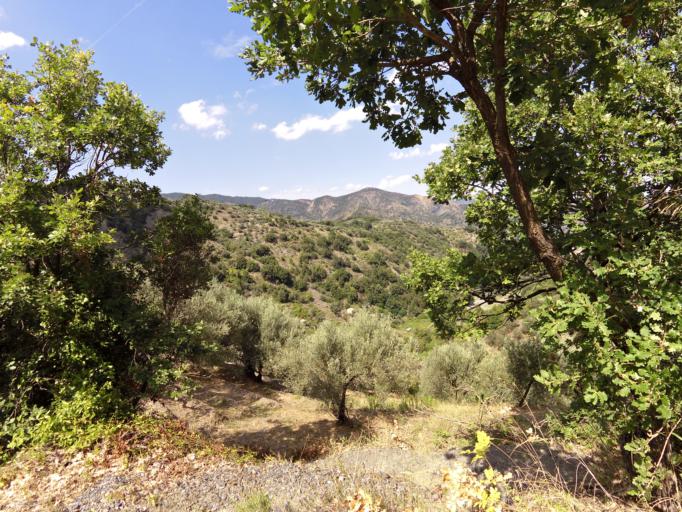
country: IT
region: Calabria
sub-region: Provincia di Reggio Calabria
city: Pazzano
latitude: 38.4722
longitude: 16.4364
